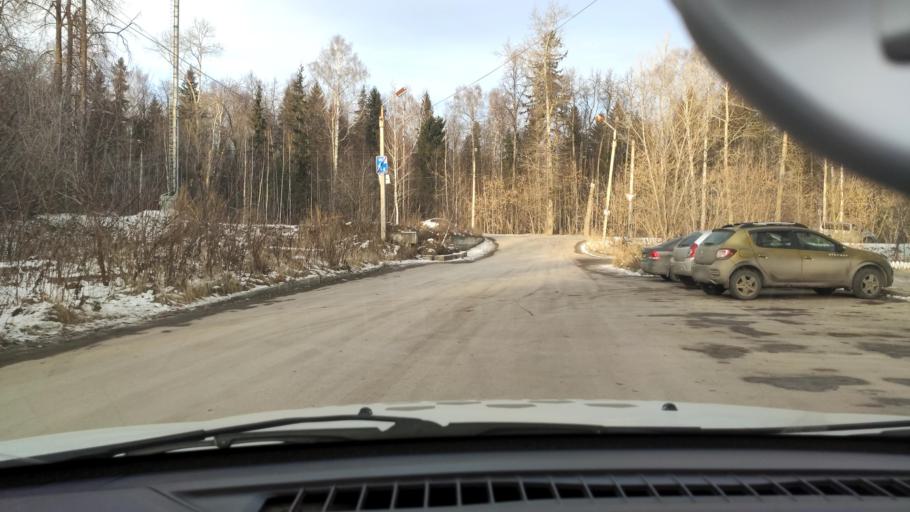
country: RU
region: Perm
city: Kondratovo
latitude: 58.0444
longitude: 56.0802
